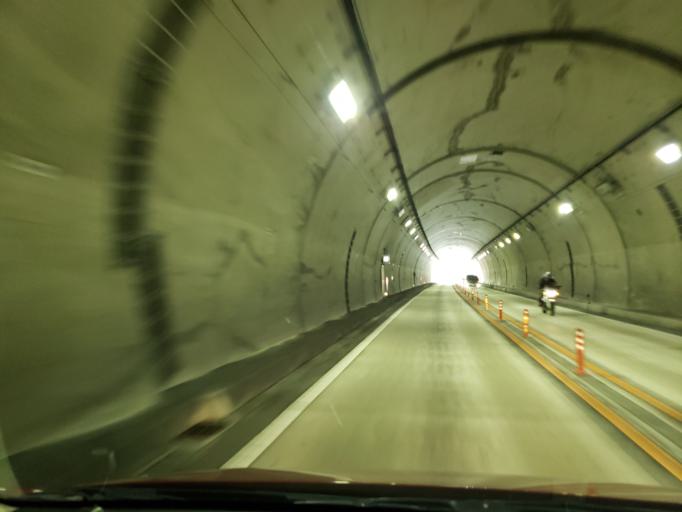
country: JP
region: Tokushima
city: Kamojimacho-jogejima
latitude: 34.1080
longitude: 134.3144
